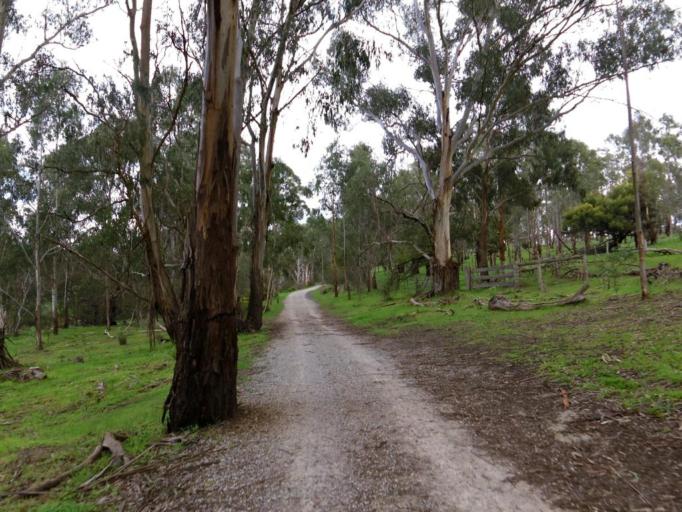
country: AU
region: Victoria
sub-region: Nillumbik
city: Eltham
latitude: -37.7360
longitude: 145.1579
